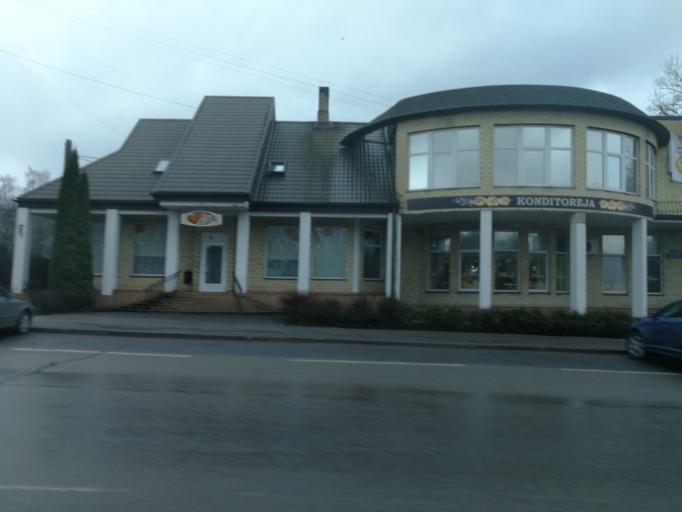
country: LV
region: Riga
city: Bolderaja
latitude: 57.0355
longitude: 24.0988
